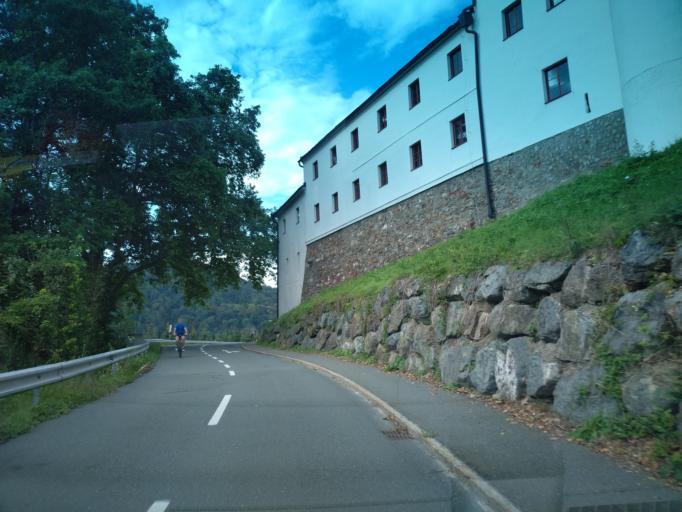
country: AT
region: Styria
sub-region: Politischer Bezirk Leibnitz
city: Leibnitz
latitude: 46.7809
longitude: 15.5234
